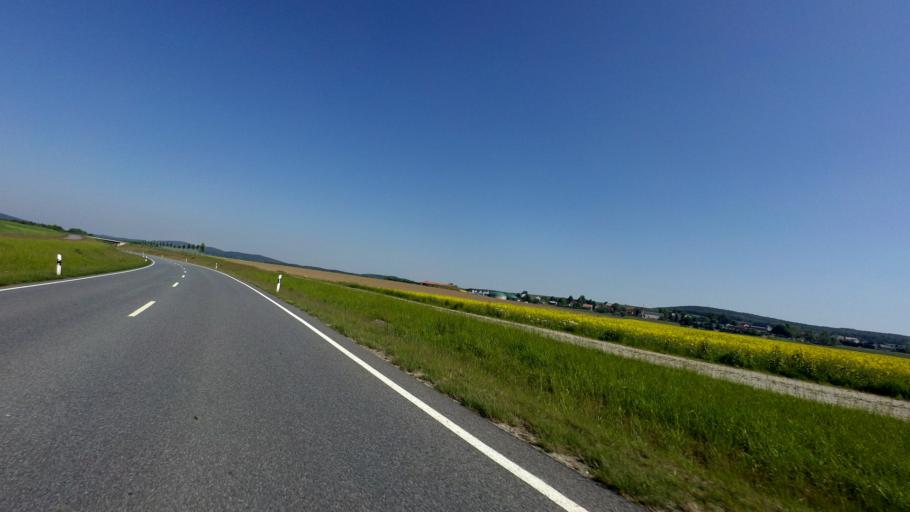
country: DE
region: Saxony
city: Bischofswerda
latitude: 51.1362
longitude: 14.1642
